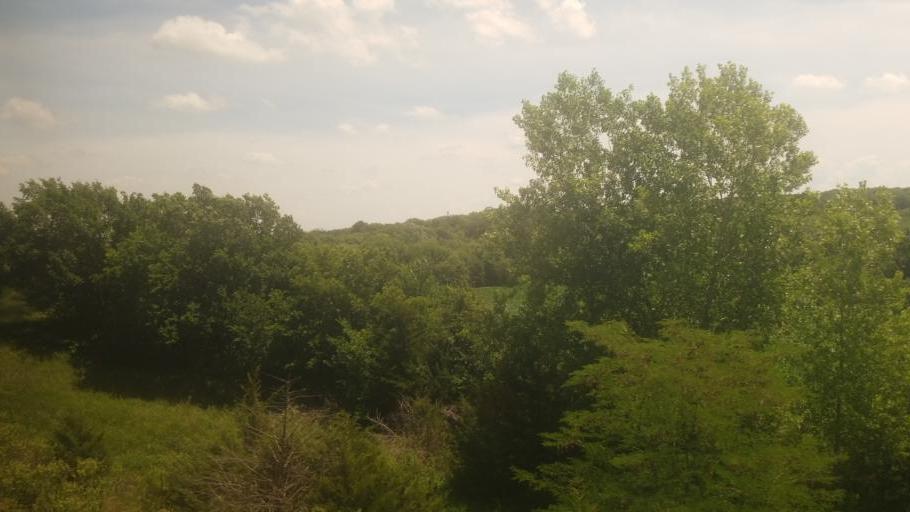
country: US
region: Missouri
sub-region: Linn County
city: Marceline
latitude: 39.8315
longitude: -92.8236
